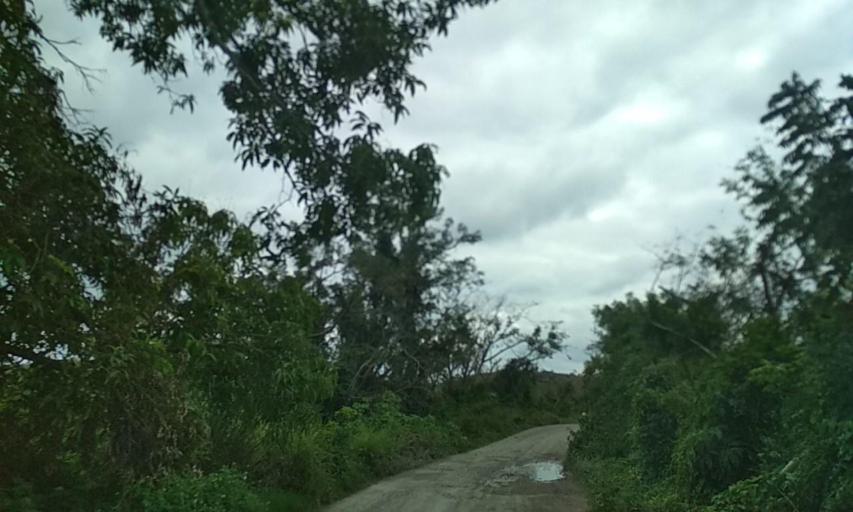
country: MX
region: Veracruz
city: Papantla de Olarte
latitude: 20.4731
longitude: -97.3099
